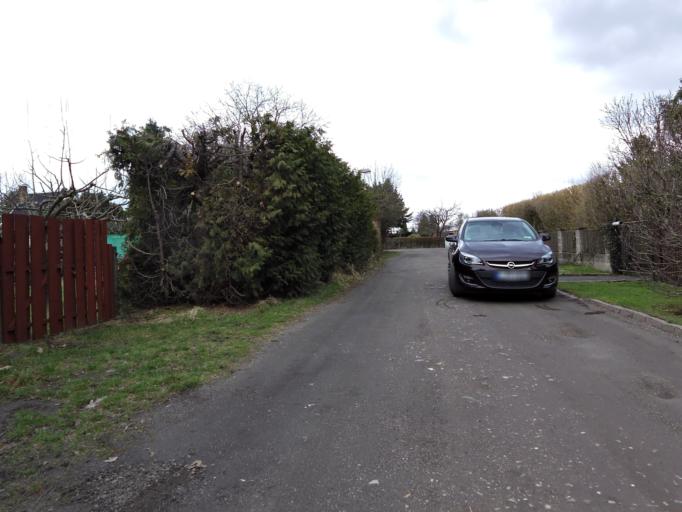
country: DE
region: Saxony
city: Markkleeberg
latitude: 51.2823
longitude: 12.4110
